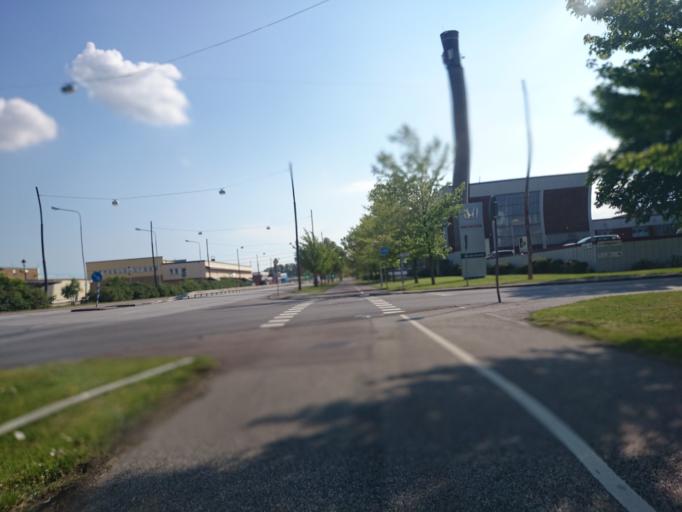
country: SE
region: Skane
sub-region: Burlovs Kommun
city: Arloev
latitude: 55.6257
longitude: 13.0634
